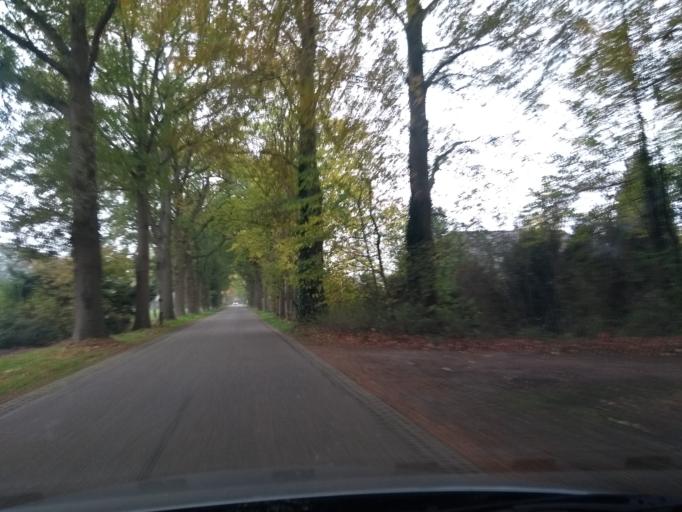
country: NL
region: Gelderland
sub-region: Gemeente Lochem
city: Almen
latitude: 52.1173
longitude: 6.3121
